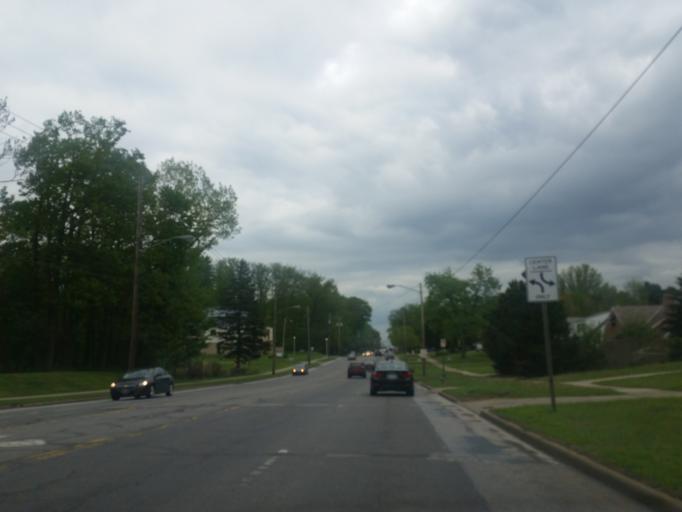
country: US
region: Ohio
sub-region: Cuyahoga County
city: South Euclid
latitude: 41.5013
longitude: -81.5126
